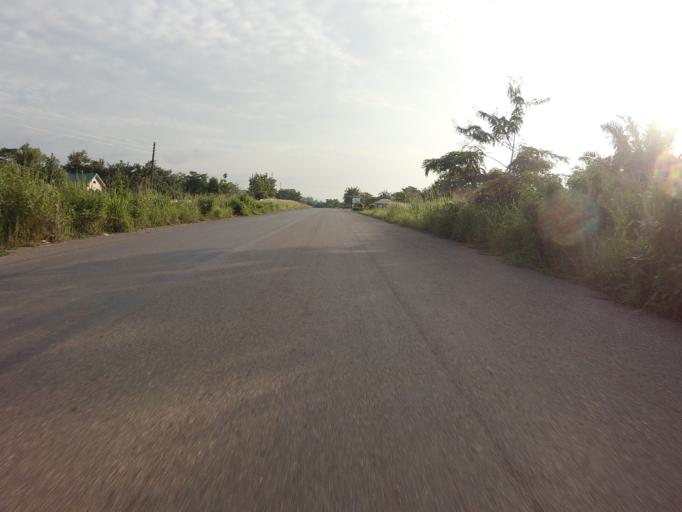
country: GH
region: Volta
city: Kpandu
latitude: 6.9049
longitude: 0.4410
